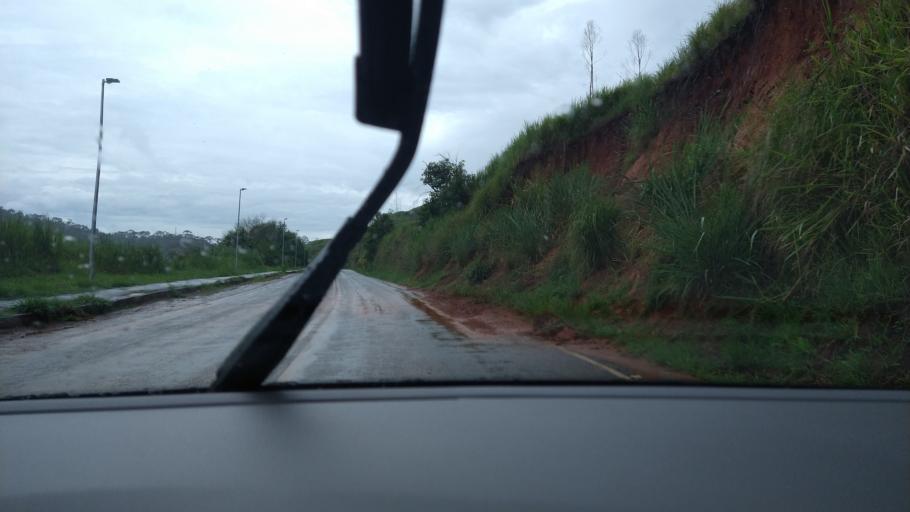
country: BR
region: Minas Gerais
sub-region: Ponte Nova
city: Ponte Nova
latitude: -20.3897
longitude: -42.9010
